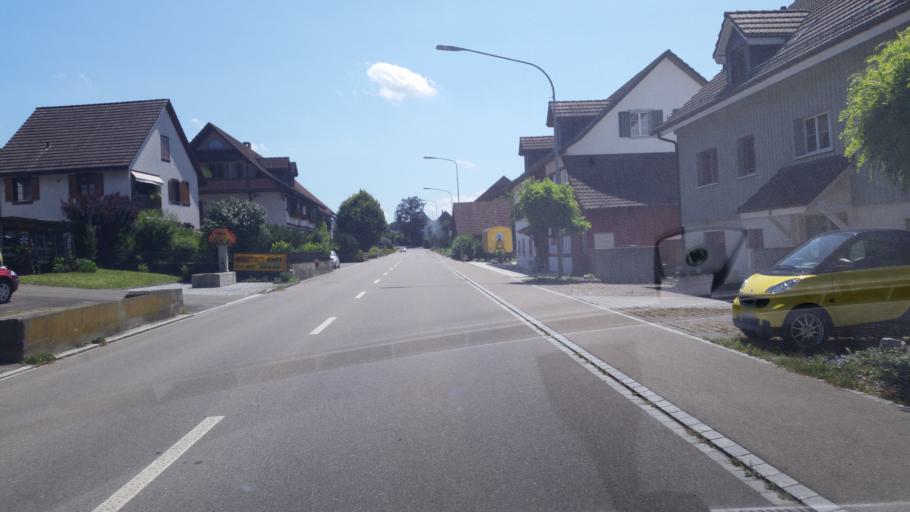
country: CH
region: Zurich
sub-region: Bezirk Buelach
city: Glattfelden
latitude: 47.5586
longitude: 8.5030
